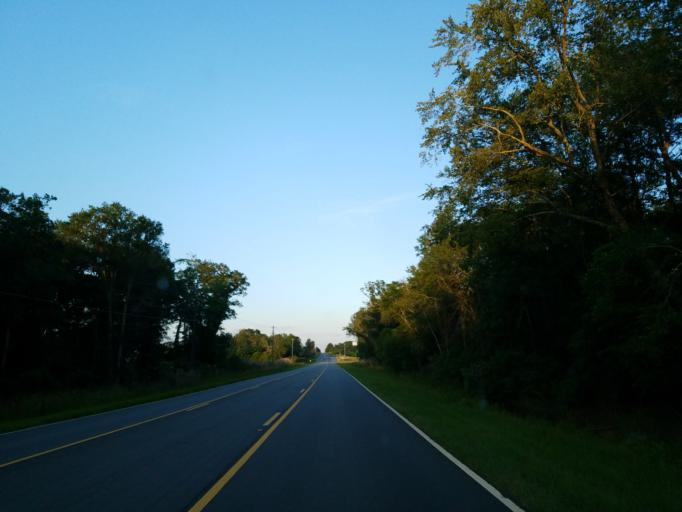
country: US
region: Georgia
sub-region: Crisp County
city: Cordele
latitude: 31.9258
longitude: -83.7516
